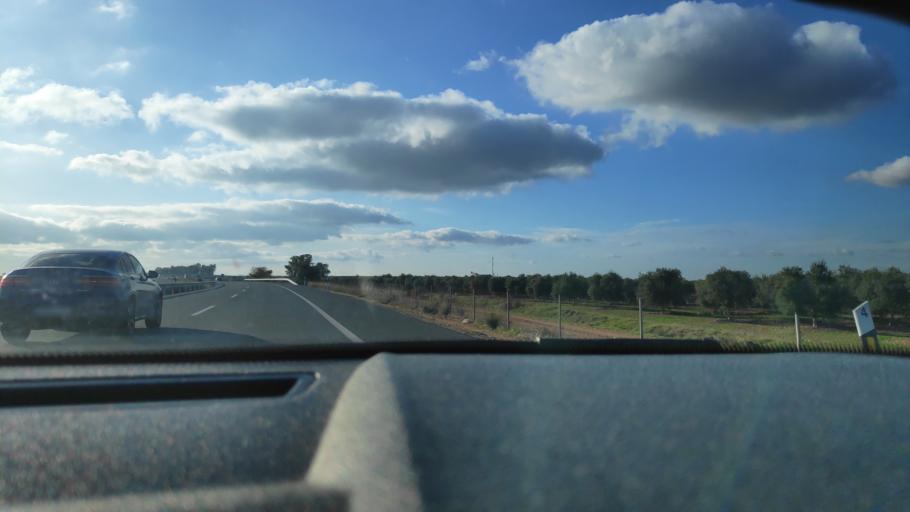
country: ES
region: Andalusia
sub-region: Provincia de Sevilla
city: La Campana
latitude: 37.4960
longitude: -5.4690
